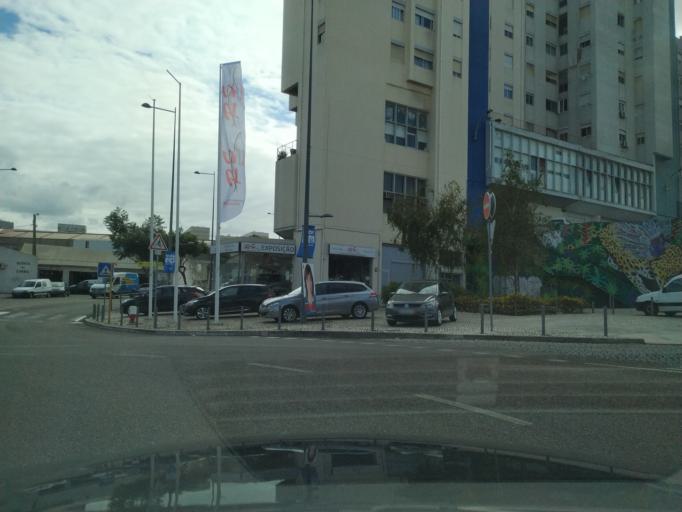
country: PT
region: Lisbon
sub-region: Loures
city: Sacavem
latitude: 38.7903
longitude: -9.1101
